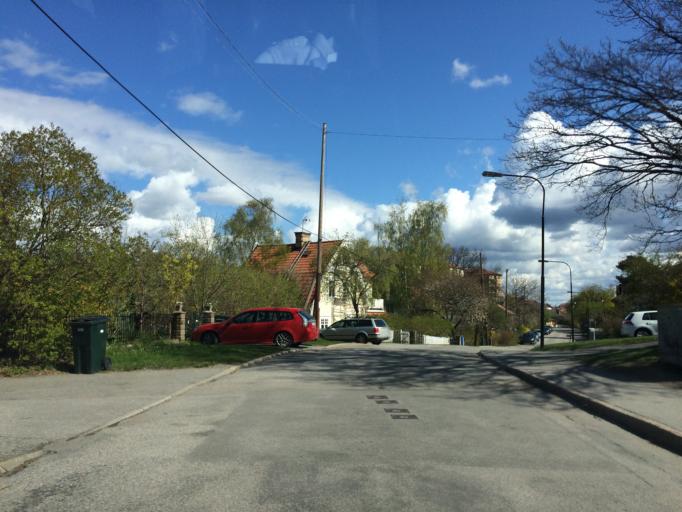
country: SE
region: Stockholm
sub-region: Huddinge Kommun
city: Segeltorp
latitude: 59.3001
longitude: 17.9513
